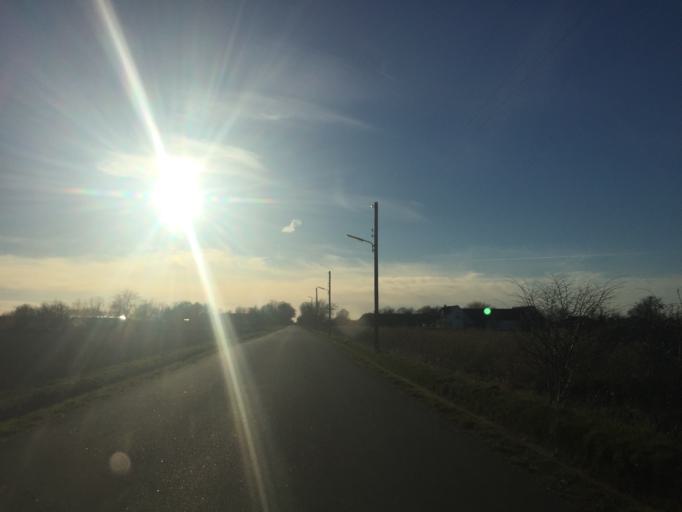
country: DK
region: Capital Region
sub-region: Dragor Kommune
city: Dragor
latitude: 55.6013
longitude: 12.6533
